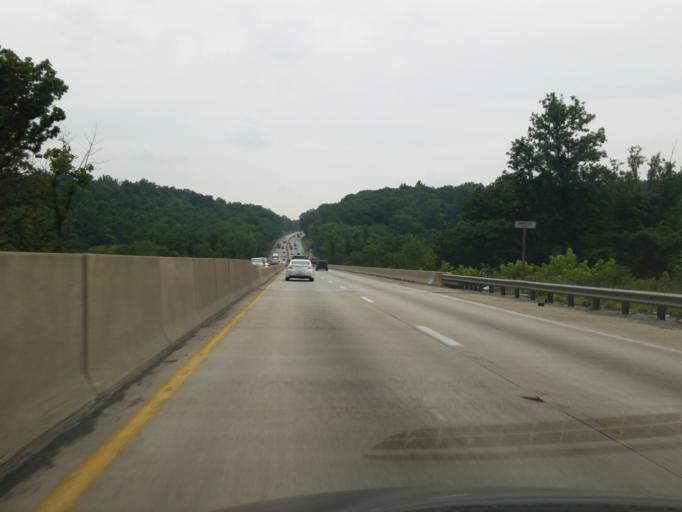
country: US
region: Pennsylvania
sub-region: York County
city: Valley Green
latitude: 40.1014
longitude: -76.7778
